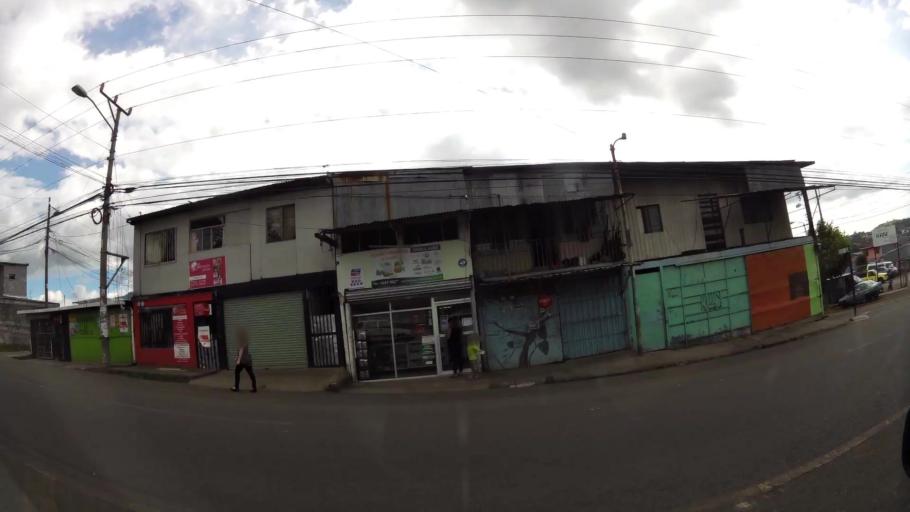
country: CR
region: Heredia
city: La Asuncion
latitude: 9.9554
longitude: -84.1541
